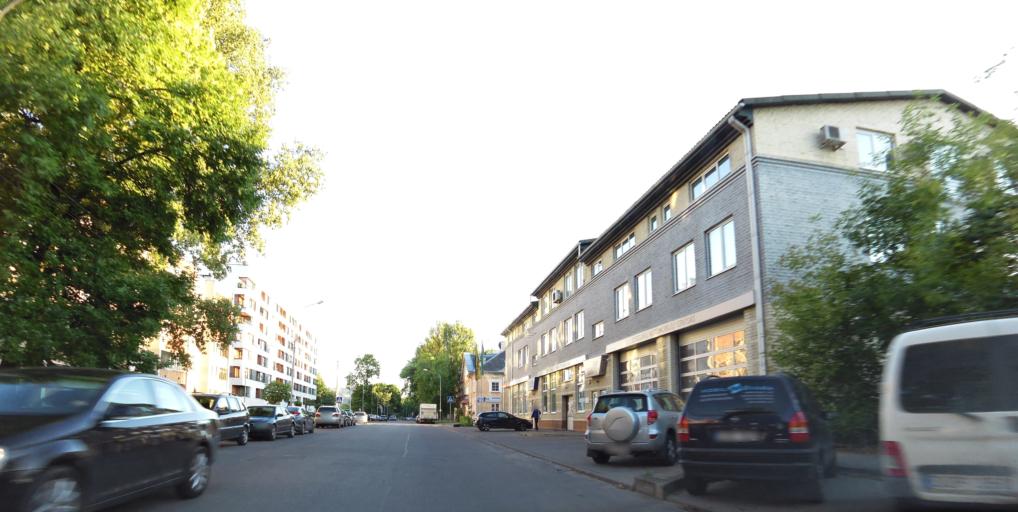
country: LT
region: Vilnius County
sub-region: Vilnius
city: Vilnius
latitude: 54.7099
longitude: 25.2900
